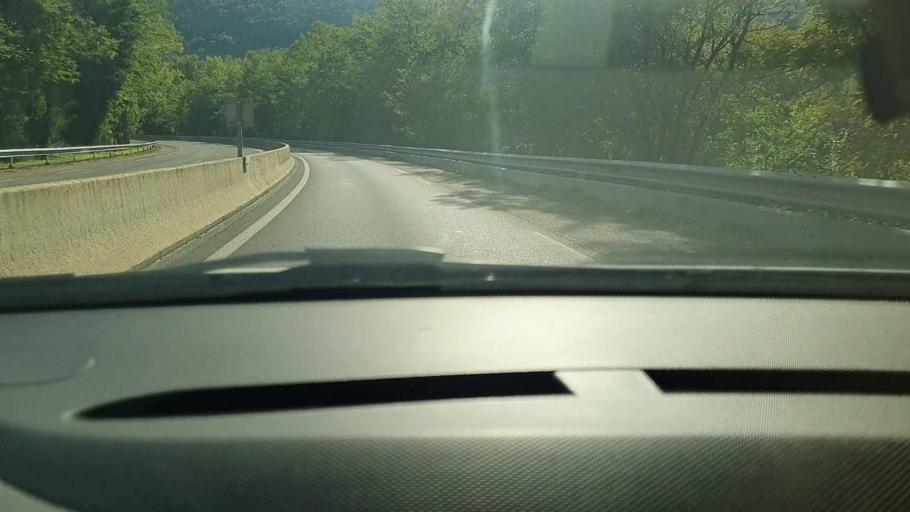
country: FR
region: Languedoc-Roussillon
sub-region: Departement du Gard
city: Molieres-sur-Ceze
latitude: 44.2632
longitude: 4.1547
